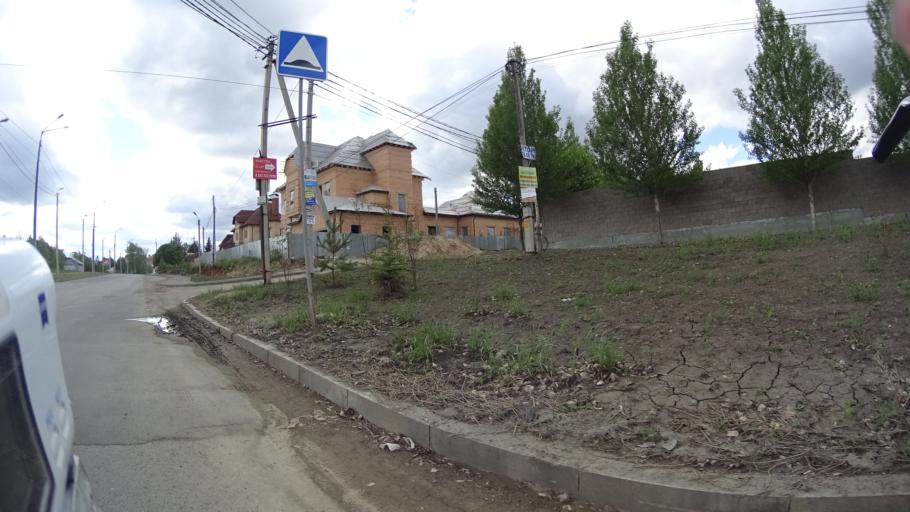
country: RU
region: Chelyabinsk
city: Sargazy
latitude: 55.1535
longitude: 61.2765
